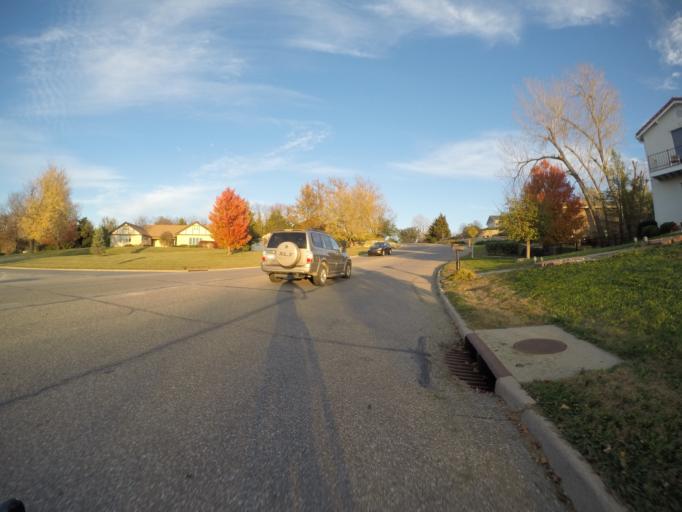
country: US
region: Kansas
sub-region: Riley County
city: Manhattan
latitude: 39.1768
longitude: -96.6136
